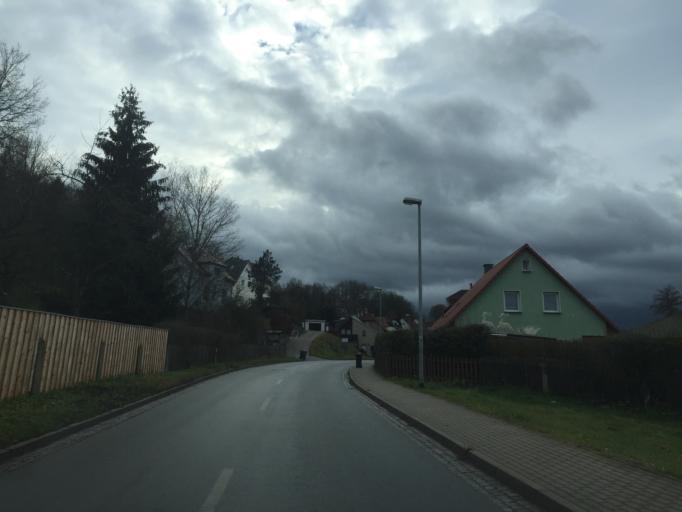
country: DE
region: Thuringia
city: Kahla
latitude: 50.7975
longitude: 11.5922
